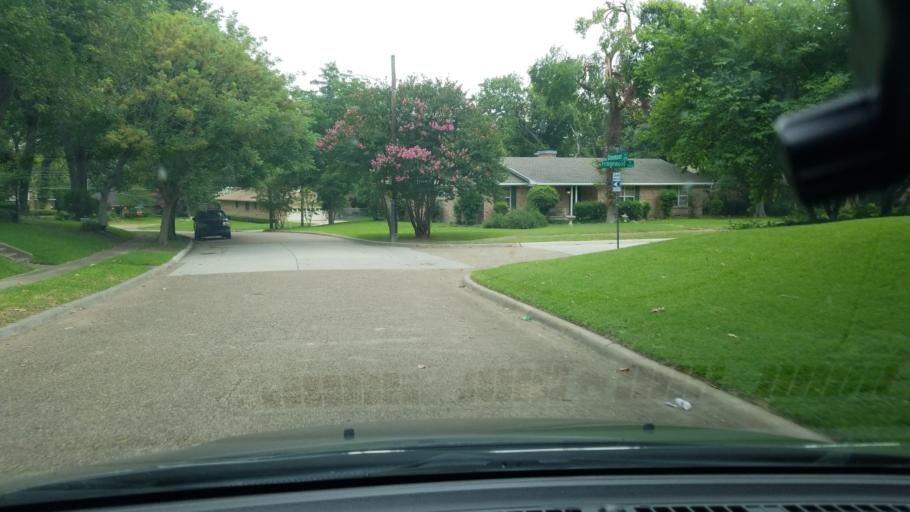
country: US
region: Texas
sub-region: Dallas County
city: Highland Park
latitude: 32.8119
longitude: -96.6954
